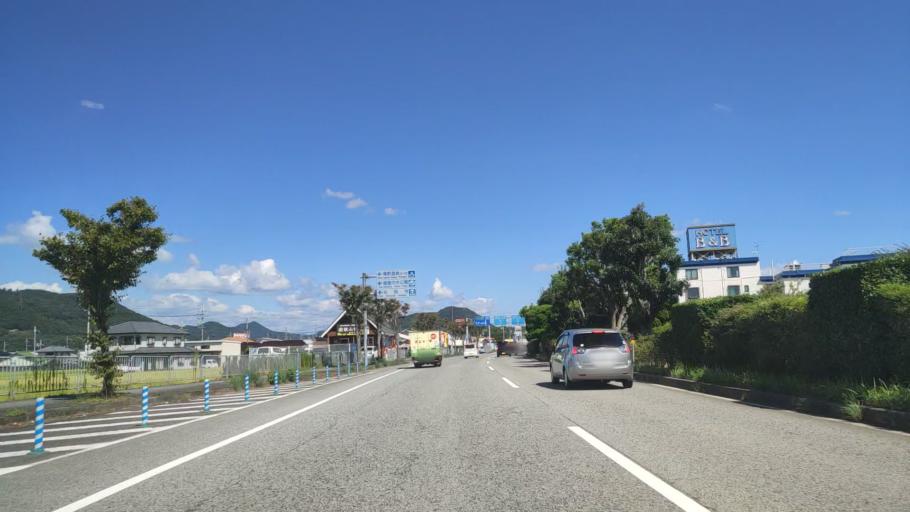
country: JP
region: Hyogo
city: Yashiro
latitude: 34.9306
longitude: 134.9596
